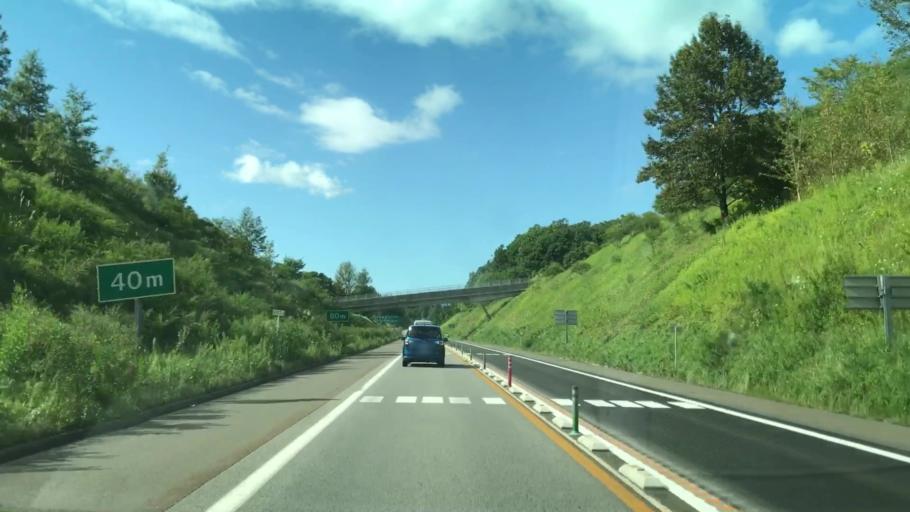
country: JP
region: Hokkaido
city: Date
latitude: 42.4378
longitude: 140.9201
